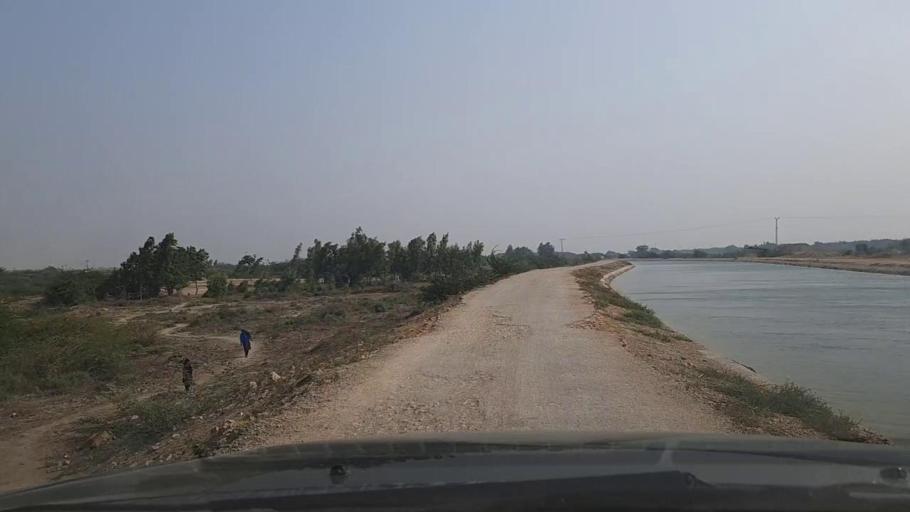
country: PK
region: Sindh
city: Thatta
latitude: 24.8026
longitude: 67.9041
